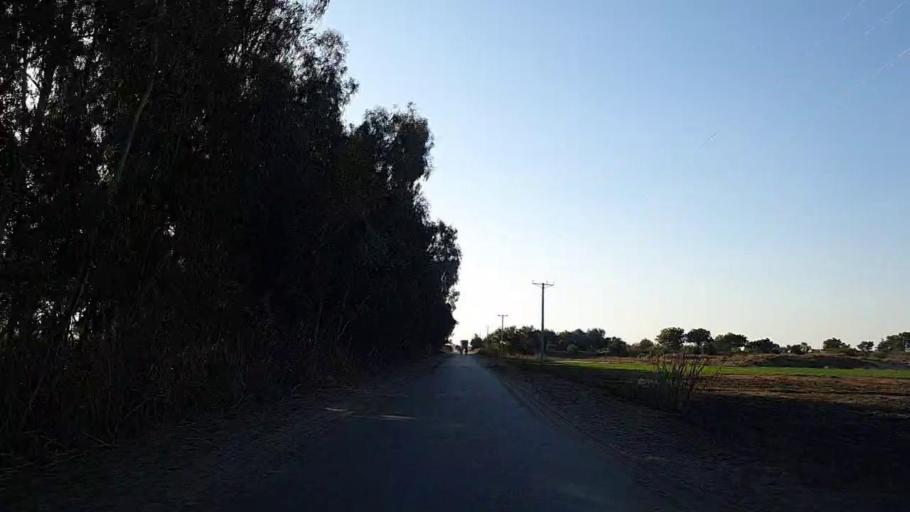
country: PK
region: Sindh
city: Sanghar
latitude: 26.2790
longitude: 68.9209
